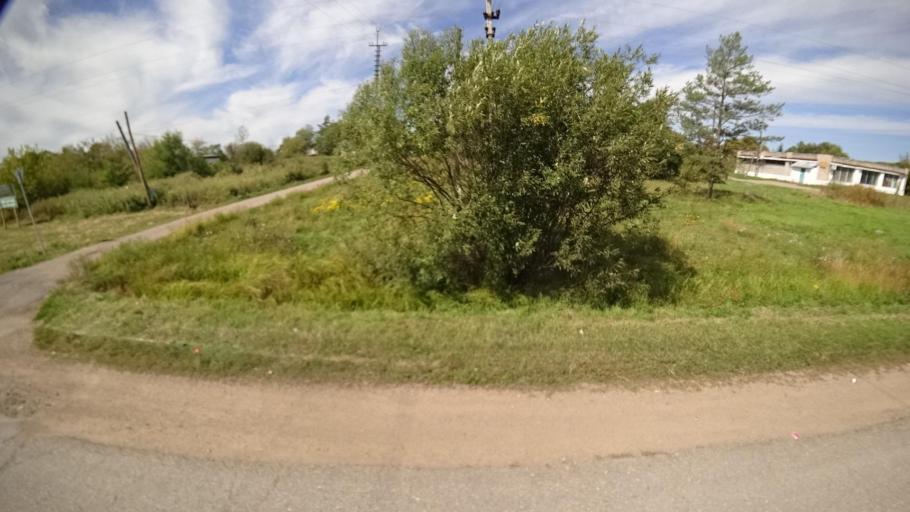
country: RU
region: Primorskiy
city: Yakovlevka
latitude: 44.6424
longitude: 133.5914
